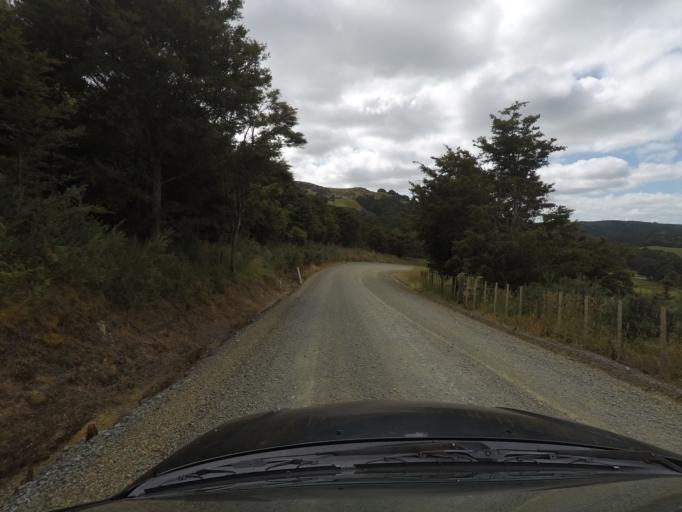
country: NZ
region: Northland
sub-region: Whangarei
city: Ruakaka
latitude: -35.9306
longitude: 174.3455
